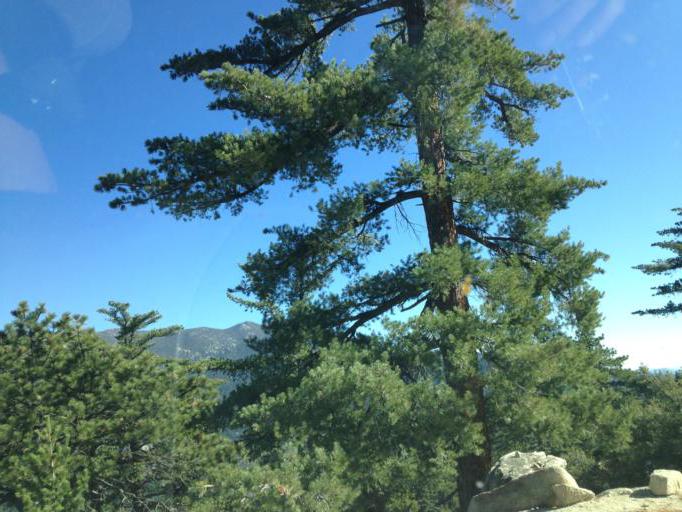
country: US
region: California
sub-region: Riverside County
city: Idyllwild-Pine Cove
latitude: 33.8235
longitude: -116.7558
